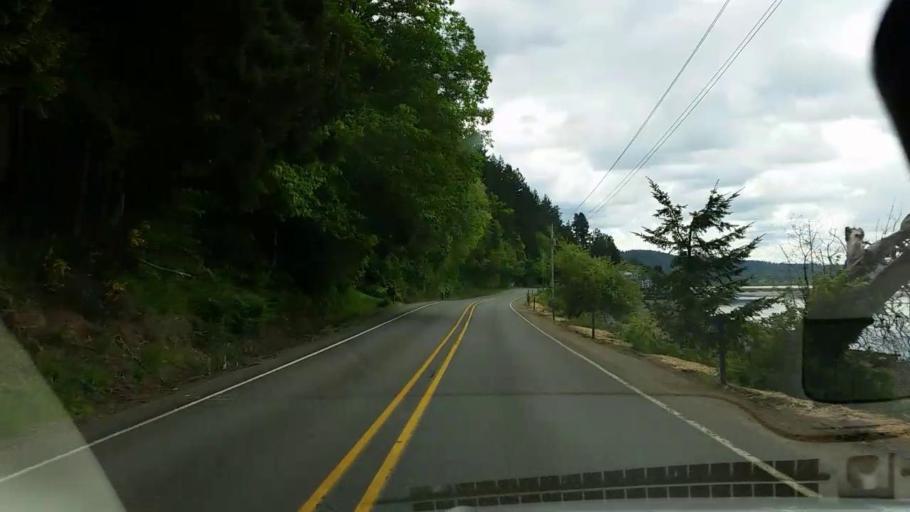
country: US
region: Washington
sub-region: Mason County
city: Shelton
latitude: 47.3516
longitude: -123.1066
